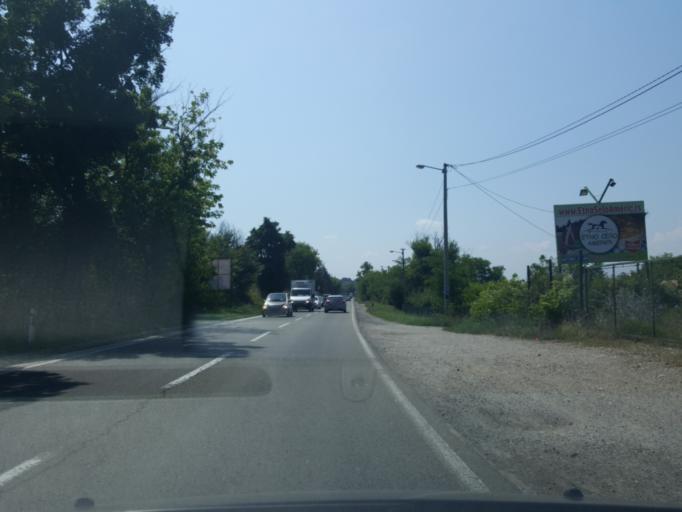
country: RS
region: Central Serbia
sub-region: Belgrade
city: Mladenovac
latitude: 44.4826
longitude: 20.6597
